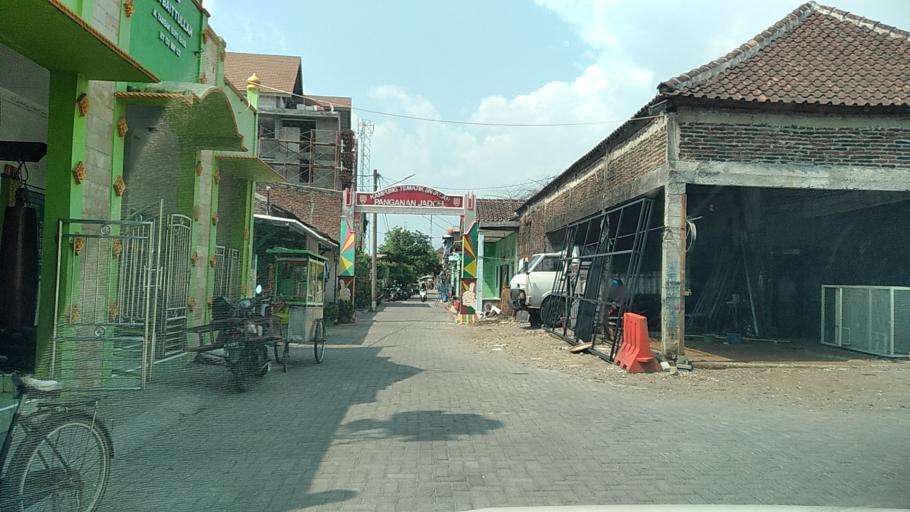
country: ID
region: Central Java
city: Semarang
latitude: -6.9846
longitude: 110.4508
